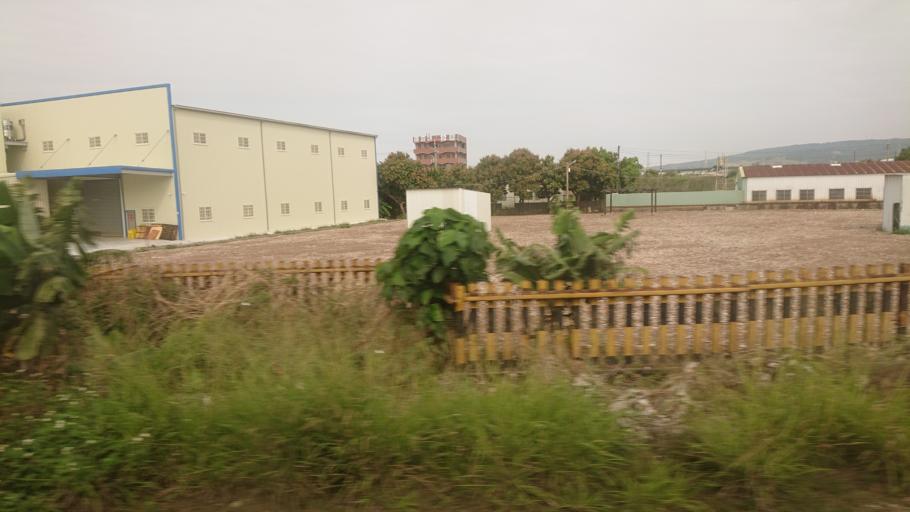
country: TW
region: Taiwan
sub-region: Changhua
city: Chang-hua
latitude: 24.0953
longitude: 120.5652
